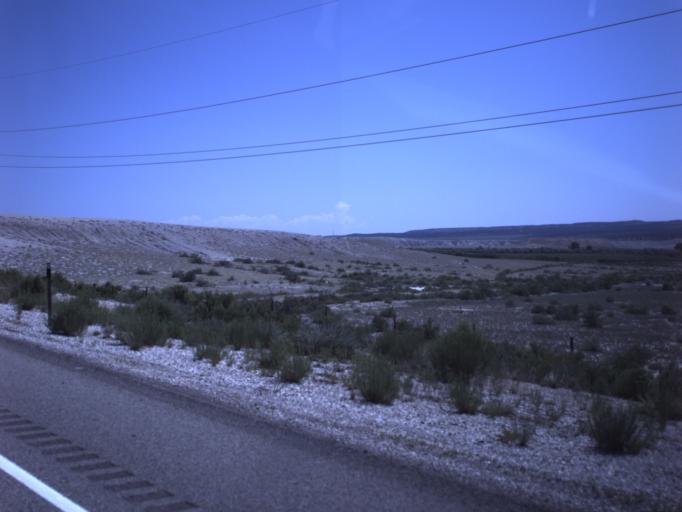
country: US
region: Utah
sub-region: Emery County
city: Ferron
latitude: 38.9263
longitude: -111.2389
